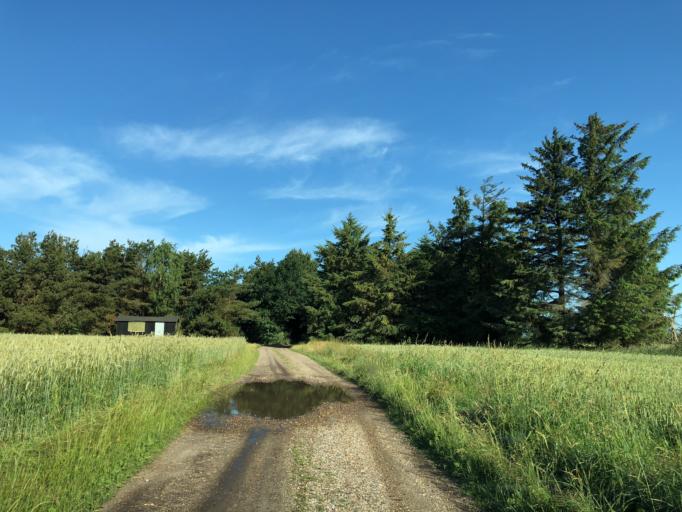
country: DK
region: Central Jutland
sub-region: Holstebro Kommune
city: Ulfborg
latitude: 56.3313
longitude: 8.2744
